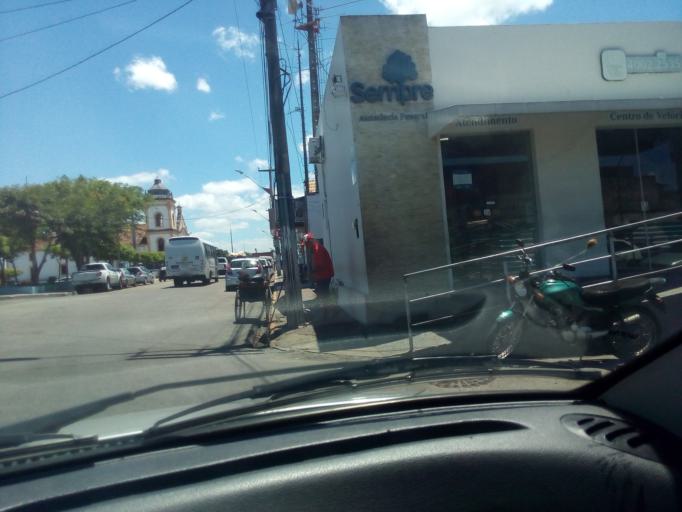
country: BR
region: Rio Grande do Norte
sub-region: Sao Goncalo Do Amarante
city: Sao Goncalo do Amarante
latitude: -5.7926
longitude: -35.3288
